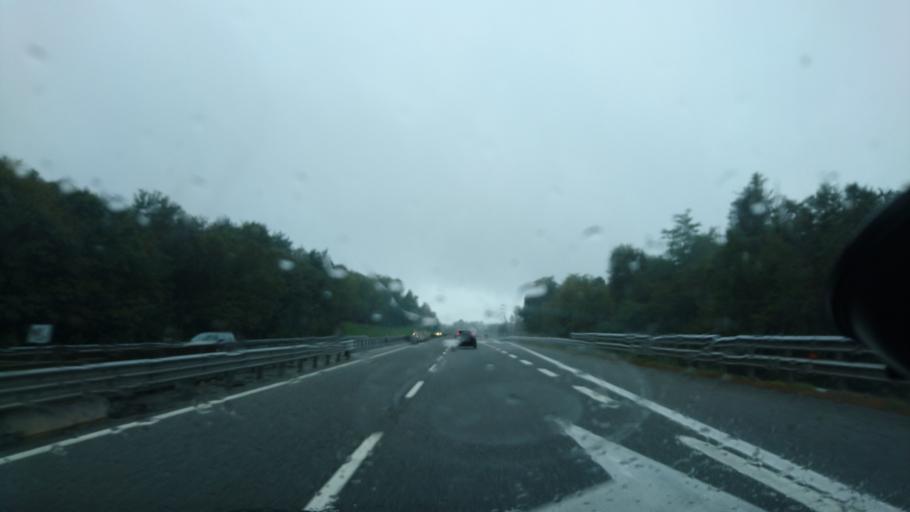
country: IT
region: Piedmont
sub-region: Provincia di Novara
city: Paruzzaro
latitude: 45.7276
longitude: 8.5165
